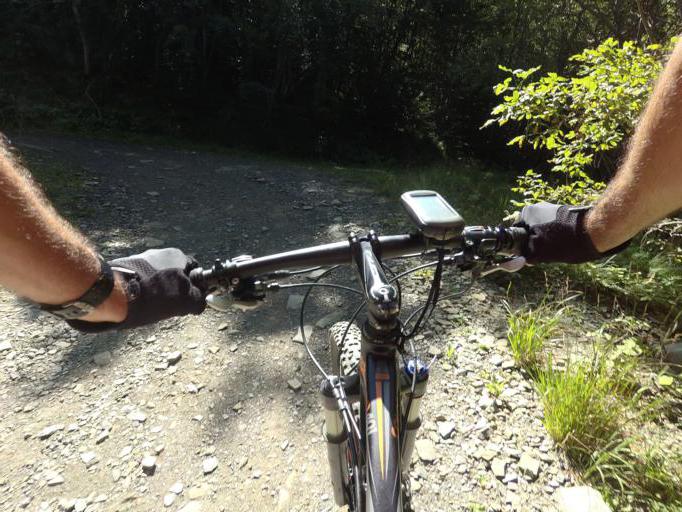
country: IT
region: Emilia-Romagna
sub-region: Provincia di Modena
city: Montecreto
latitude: 44.2279
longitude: 10.7291
